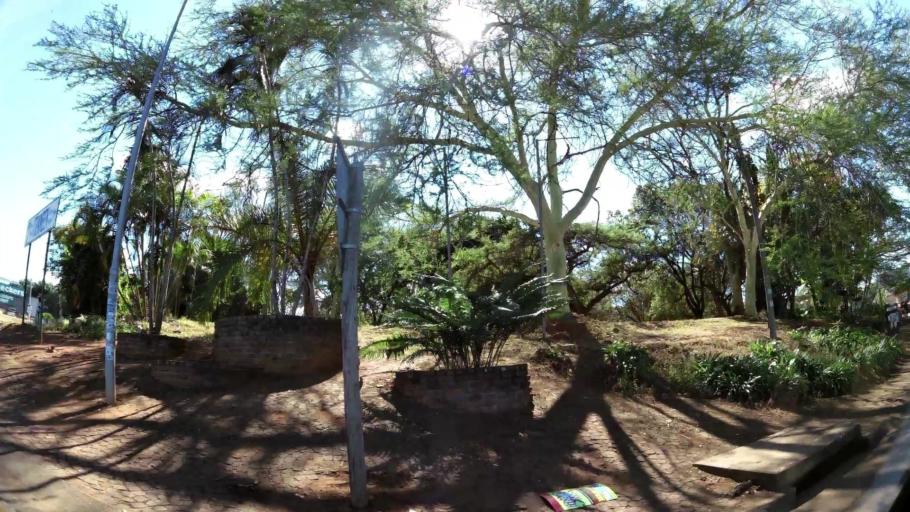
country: ZA
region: Limpopo
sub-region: Mopani District Municipality
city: Tzaneen
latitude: -23.8228
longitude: 30.1591
